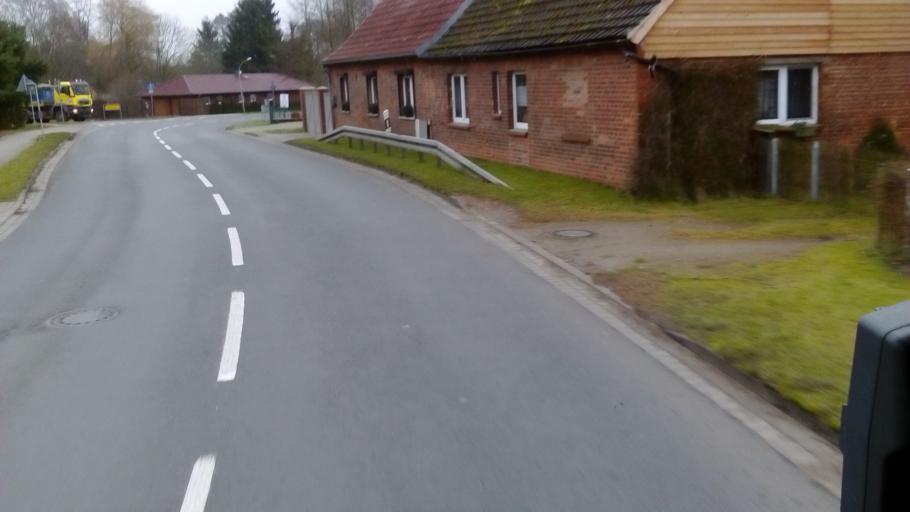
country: DE
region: Brandenburg
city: Heiligengrabe
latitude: 53.1390
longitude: 12.3455
